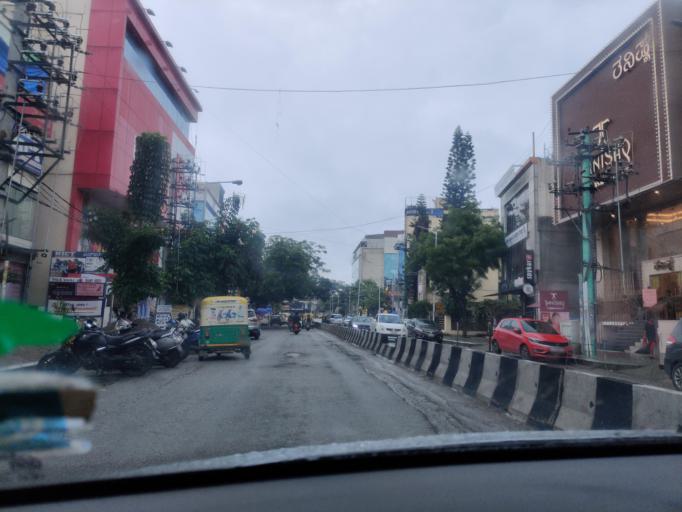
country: IN
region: Karnataka
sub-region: Bangalore Urban
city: Bangalore
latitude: 13.0246
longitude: 77.6371
